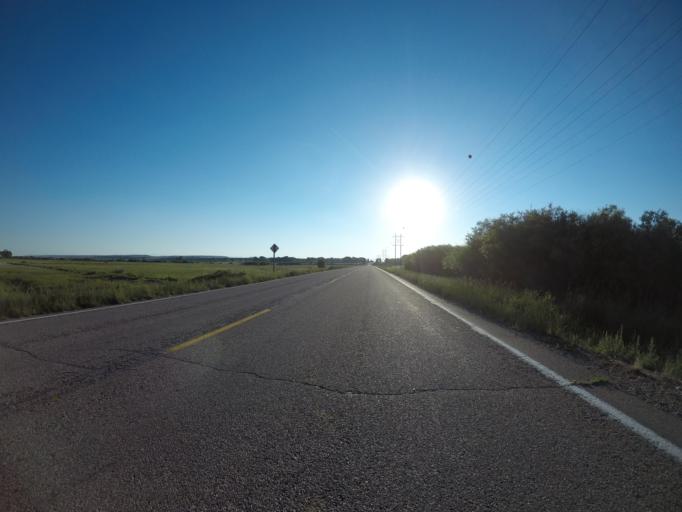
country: US
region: Wyoming
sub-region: Sublette County
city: Marbleton
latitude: 42.5727
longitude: -109.9431
